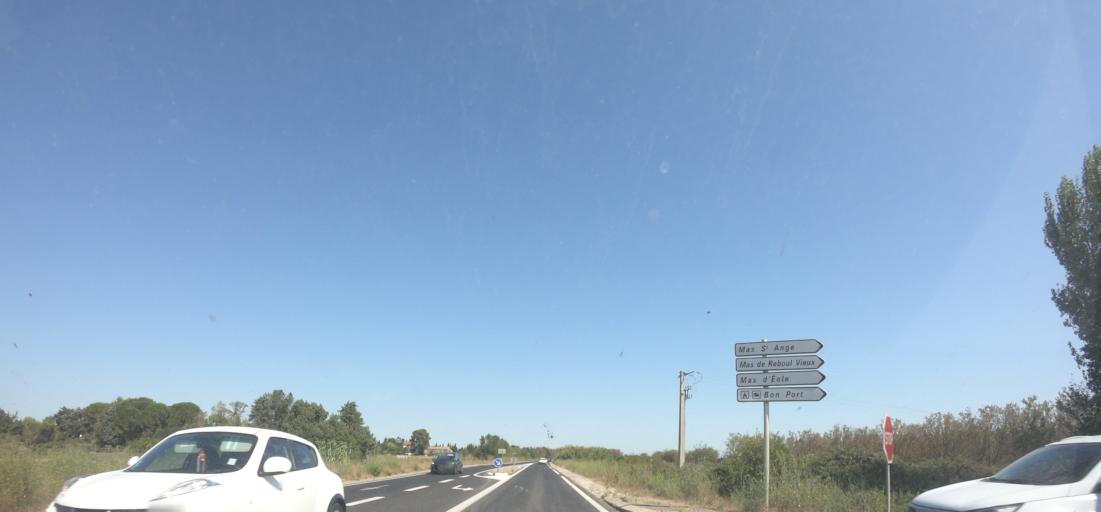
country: FR
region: Languedoc-Roussillon
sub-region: Departement de l'Herault
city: Lunel
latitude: 43.6564
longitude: 4.1383
